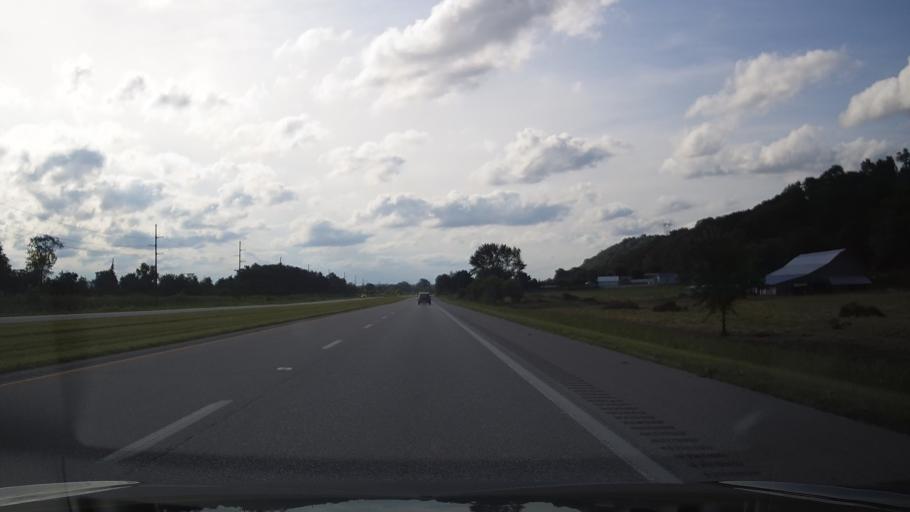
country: US
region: Kentucky
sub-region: Greenup County
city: Greenup
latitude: 38.6042
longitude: -82.8205
